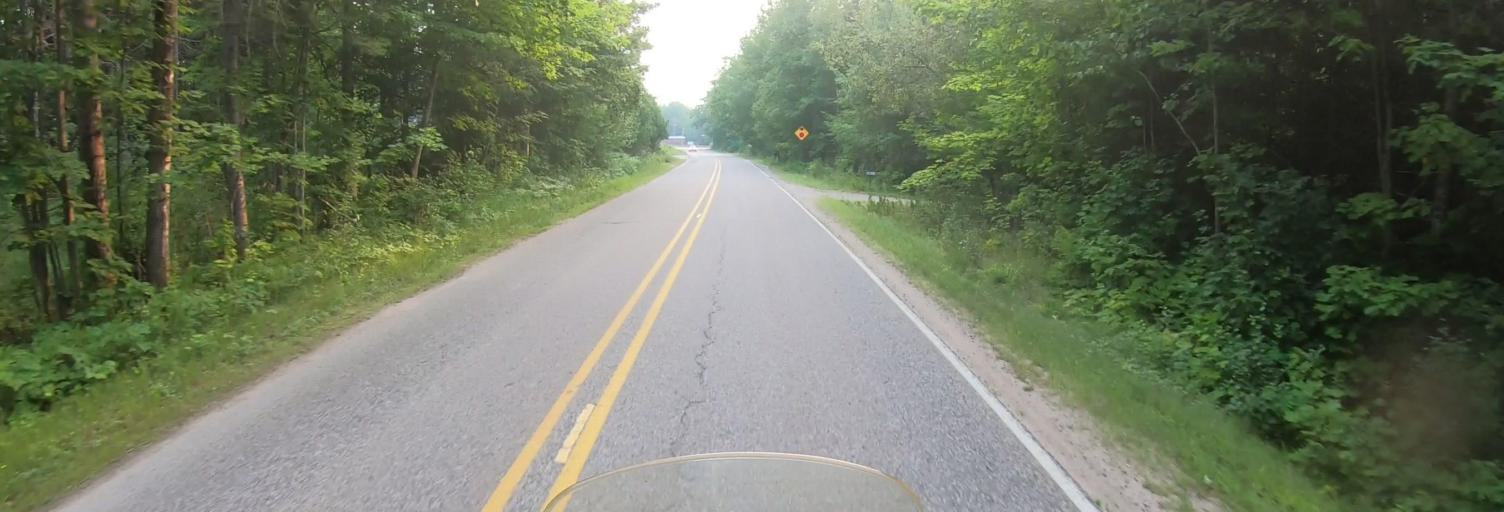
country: US
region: Michigan
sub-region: Chippewa County
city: Sault Ste. Marie
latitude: 46.4623
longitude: -84.7361
